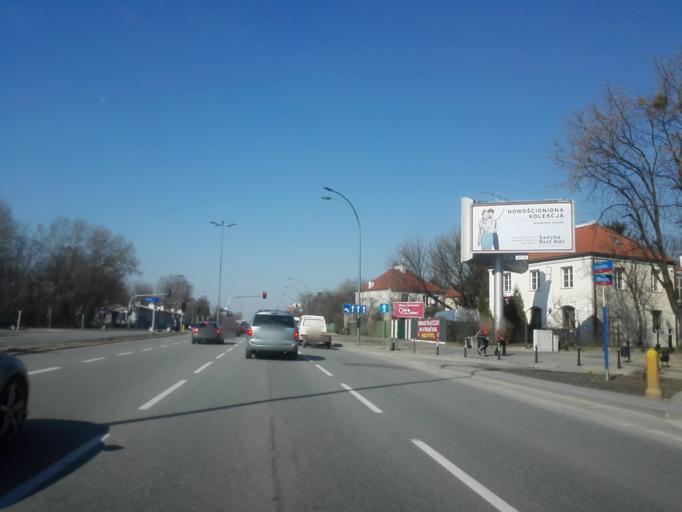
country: PL
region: Masovian Voivodeship
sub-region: Warszawa
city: Wilanow
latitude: 52.1814
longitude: 21.0698
